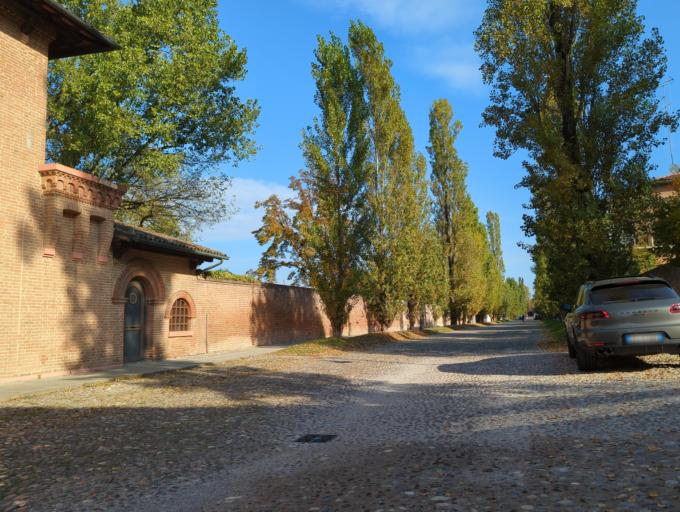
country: IT
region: Emilia-Romagna
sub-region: Provincia di Ferrara
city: Ferrara
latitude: 44.8456
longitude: 11.6228
